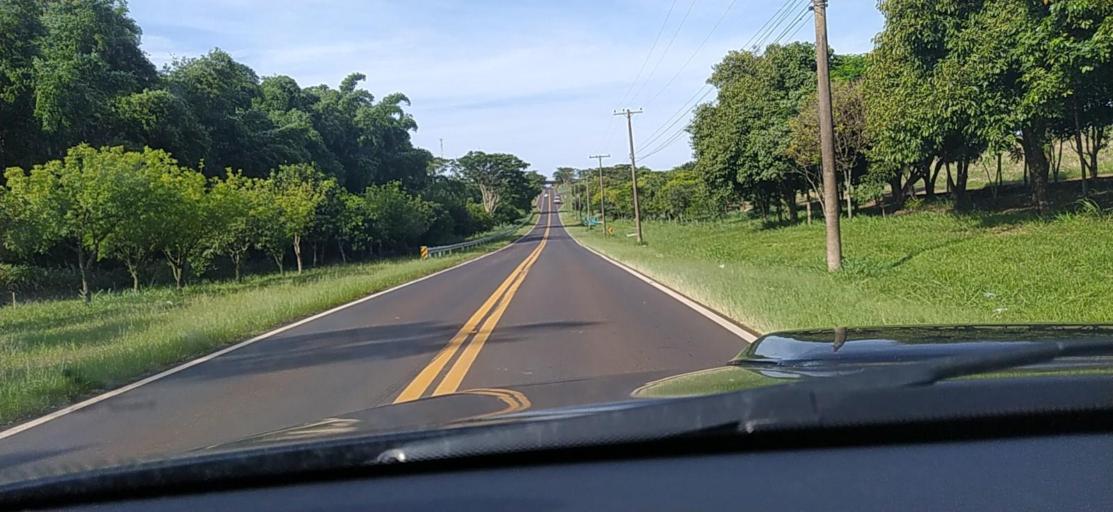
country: BR
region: Sao Paulo
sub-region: Pindorama
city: Pindorama
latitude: -21.2029
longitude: -48.9269
